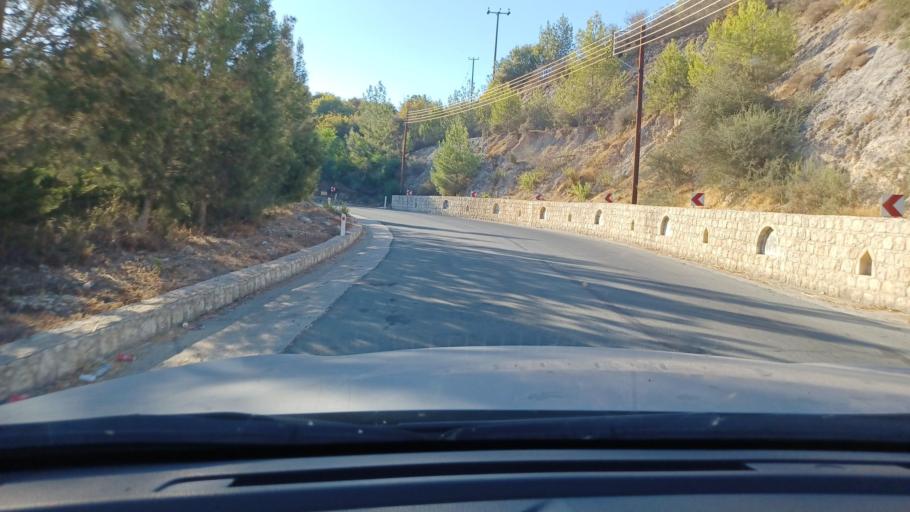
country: CY
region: Pafos
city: Polis
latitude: 34.9848
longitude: 32.4869
